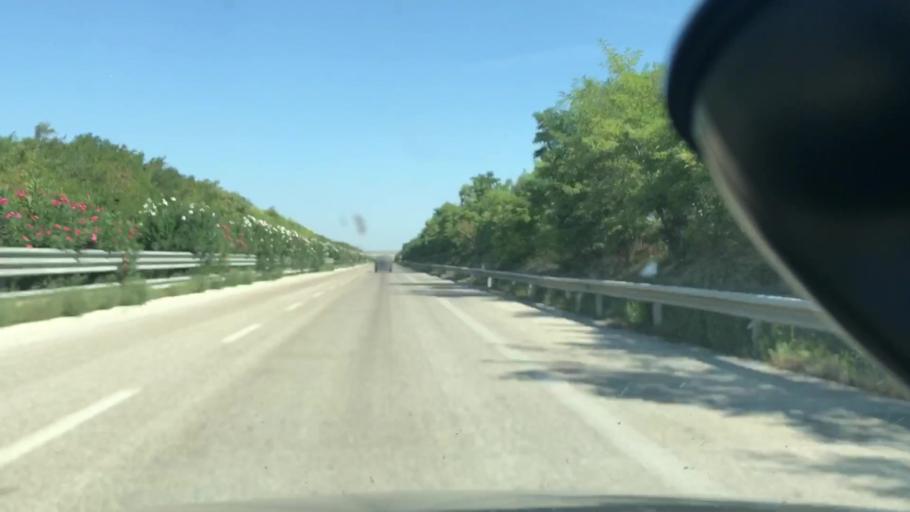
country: IT
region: Apulia
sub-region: Provincia di Foggia
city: Ascoli Satriano
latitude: 41.2831
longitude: 15.5540
